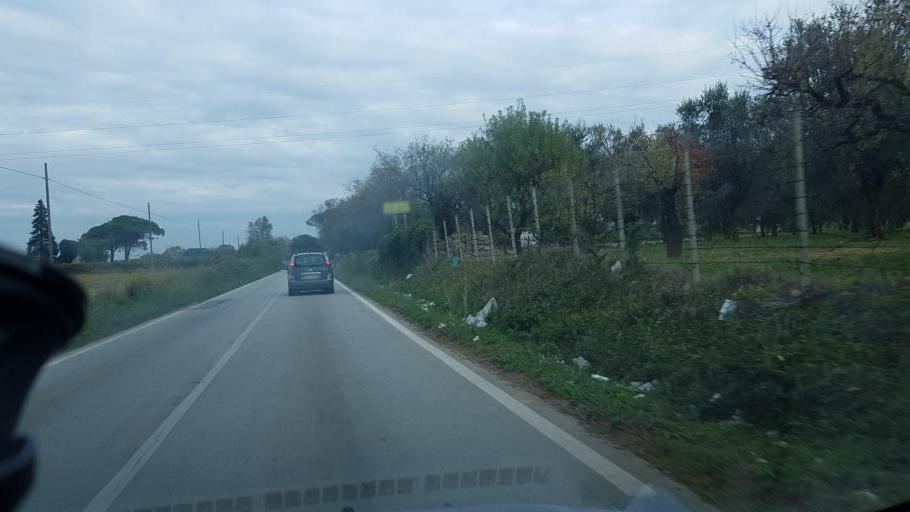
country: IT
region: Apulia
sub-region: Provincia di Brindisi
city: Francavilla Fontana
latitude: 40.5174
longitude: 17.6097
